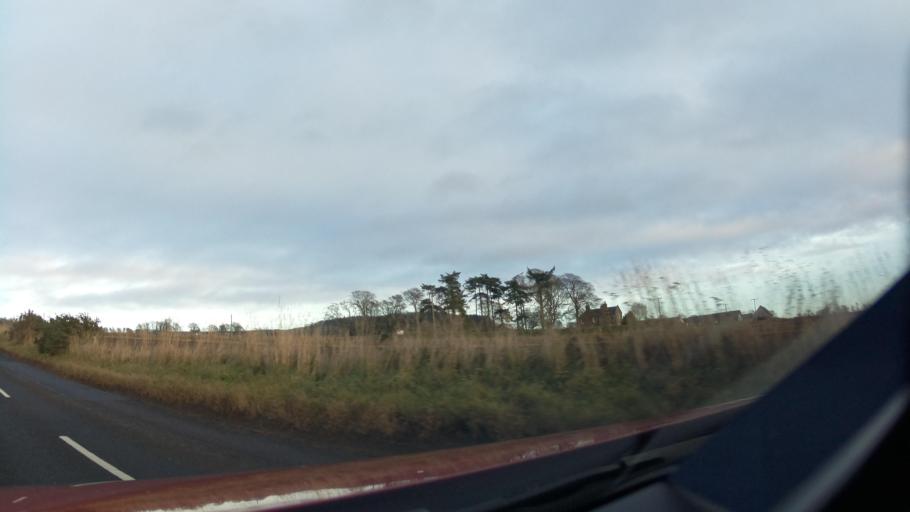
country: GB
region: Scotland
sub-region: Fife
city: Tayport
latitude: 56.5195
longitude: -2.8156
